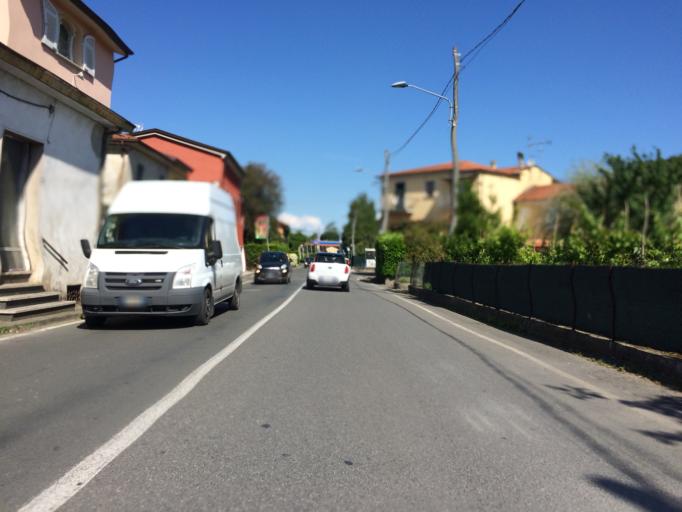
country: IT
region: Liguria
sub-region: Provincia di La Spezia
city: Sarzana
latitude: 44.1052
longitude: 9.9749
